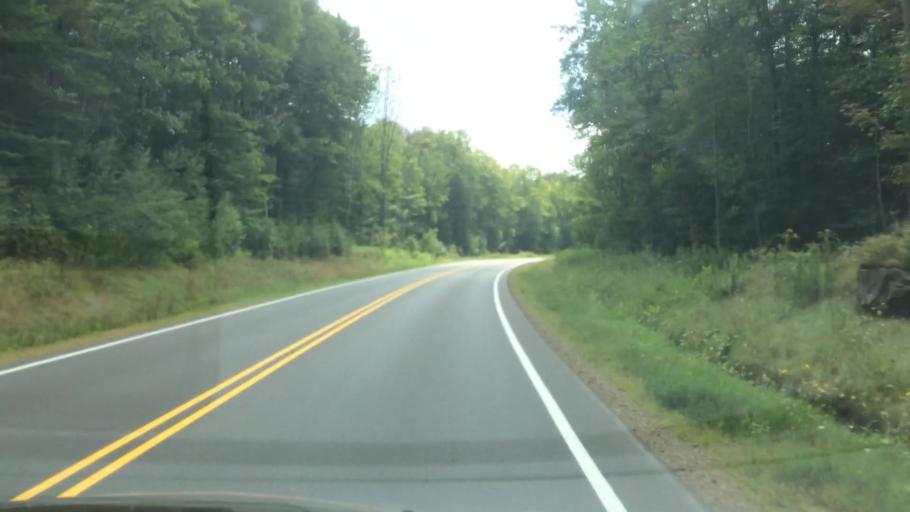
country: US
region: Pennsylvania
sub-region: McKean County
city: Bradford
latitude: 41.8826
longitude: -78.5784
